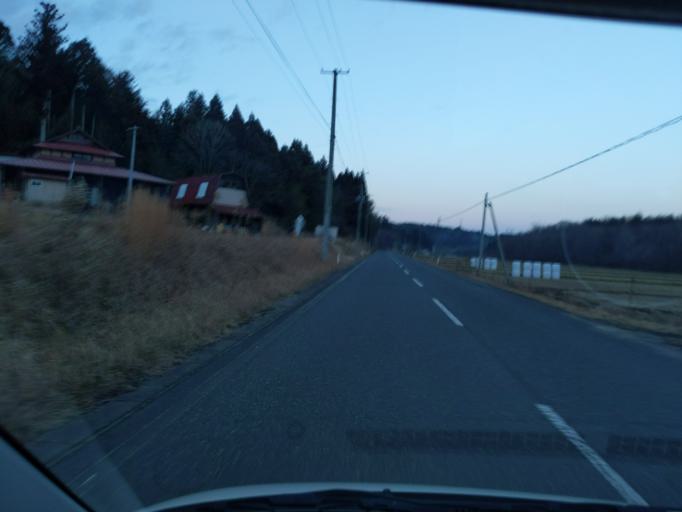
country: JP
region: Iwate
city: Ichinoseki
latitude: 38.8261
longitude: 141.1177
